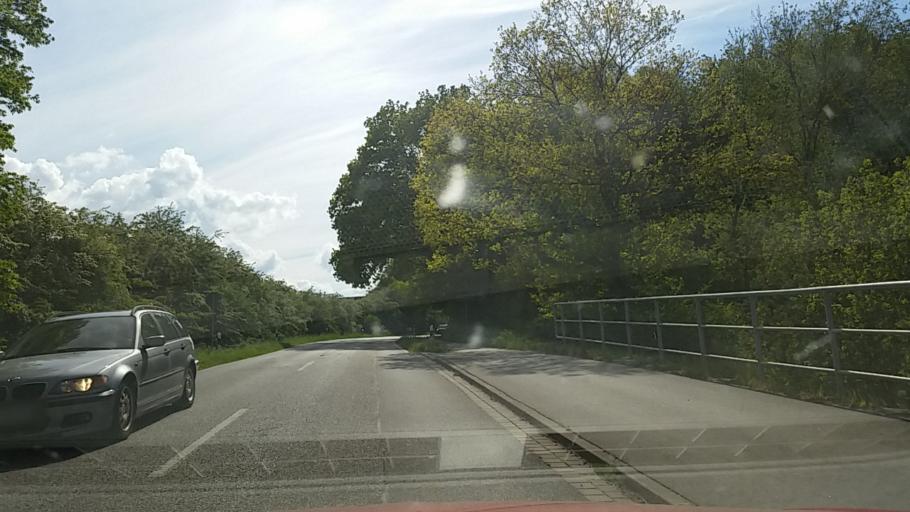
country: DE
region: Schleswig-Holstein
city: Meddewade
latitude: 53.8173
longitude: 10.4288
